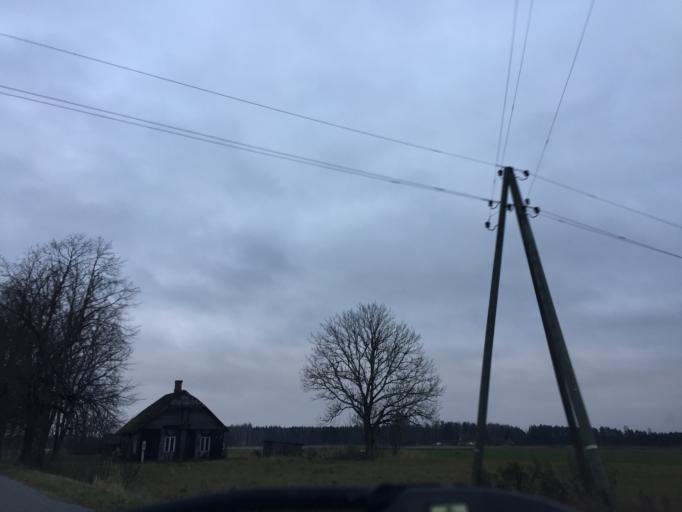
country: LV
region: Aloja
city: Aloja
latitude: 57.6904
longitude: 24.8864
